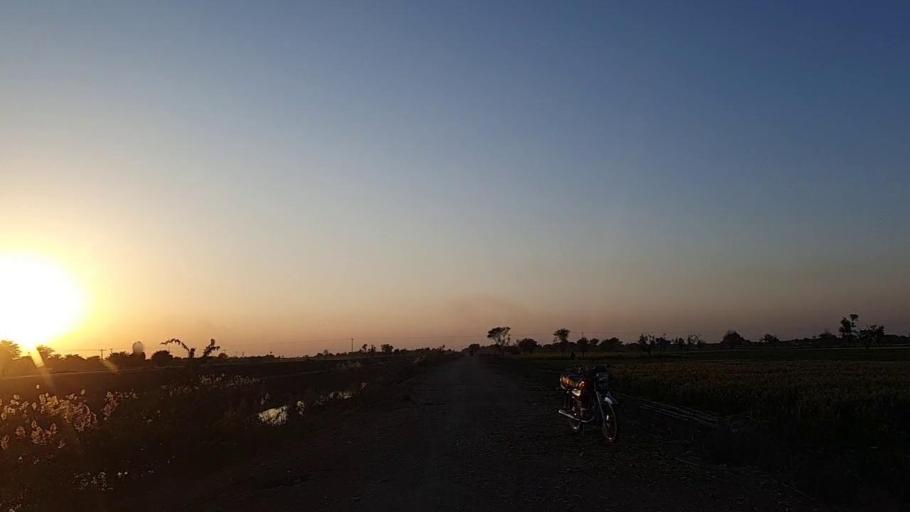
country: PK
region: Sindh
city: Jam Sahib
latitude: 26.3102
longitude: 68.6608
